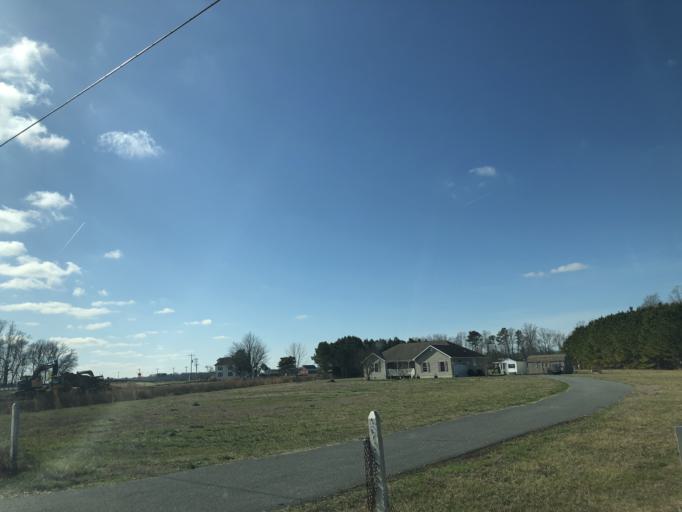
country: US
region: Maryland
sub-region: Worcester County
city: Snow Hill
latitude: 38.2294
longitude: -75.3393
